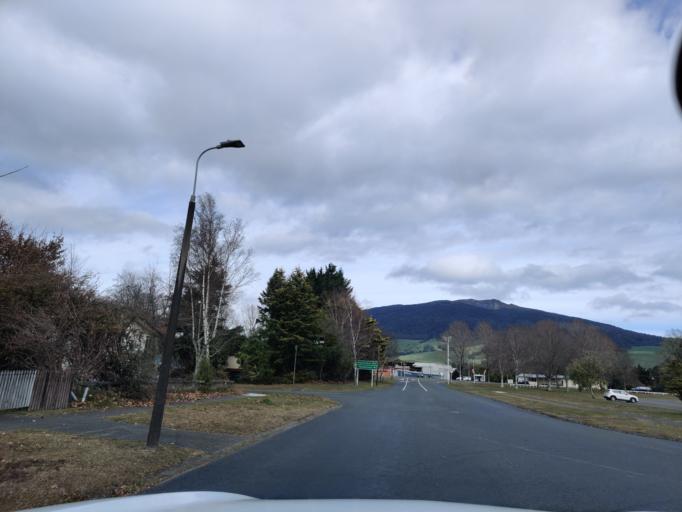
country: NZ
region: Waikato
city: Turangi
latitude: -38.9942
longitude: 175.8034
